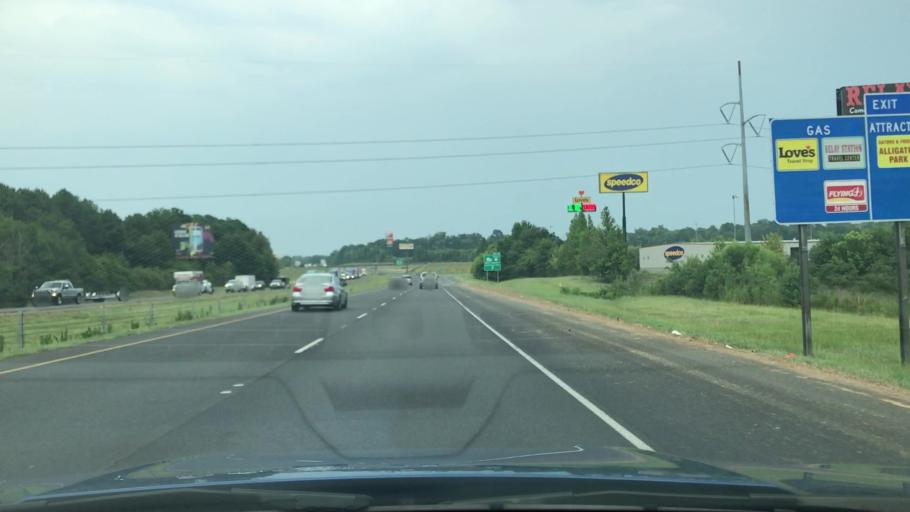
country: US
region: Louisiana
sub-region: Caddo Parish
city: Greenwood
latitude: 32.4485
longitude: -93.9867
